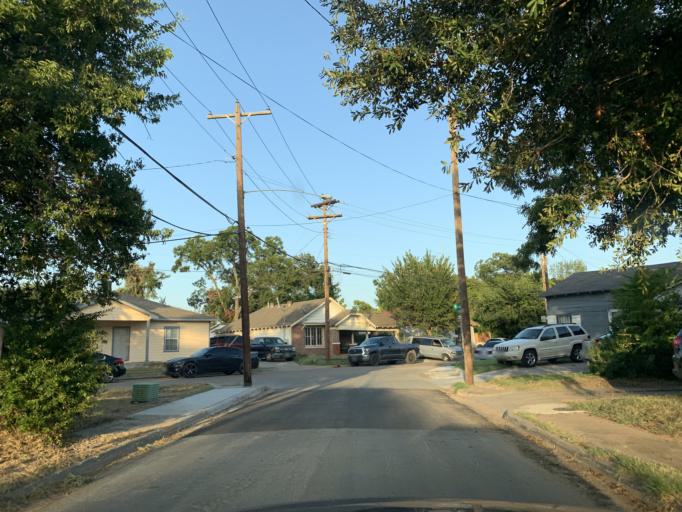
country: US
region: Texas
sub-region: Dallas County
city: Dallas
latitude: 32.7538
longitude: -96.7518
